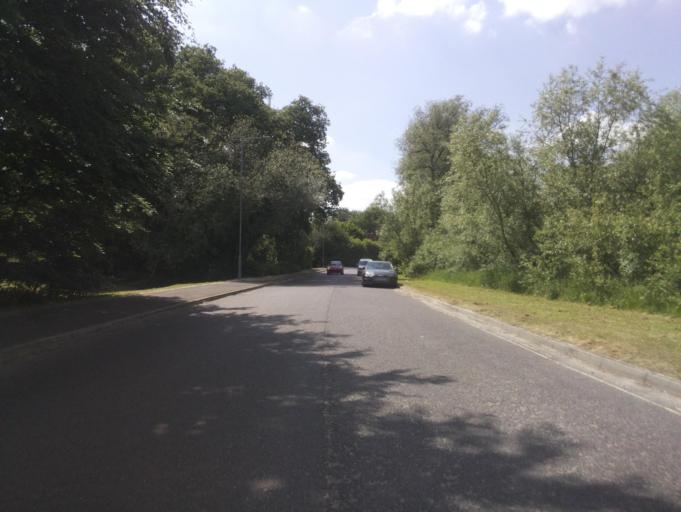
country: GB
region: England
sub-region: Wiltshire
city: Pewsey
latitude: 51.3436
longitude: -1.7738
